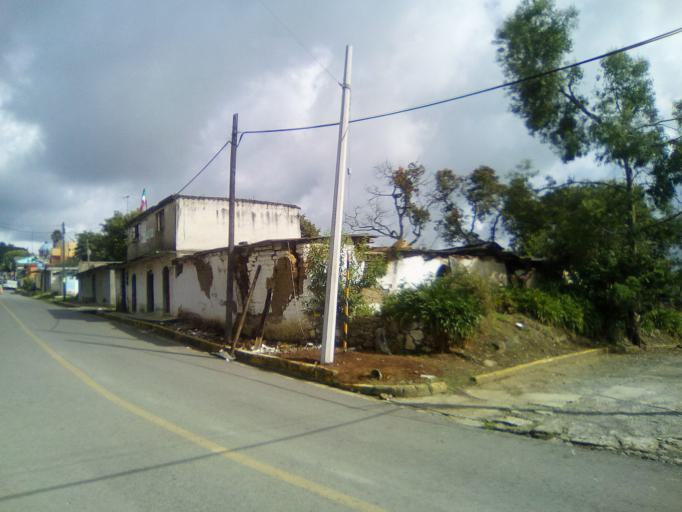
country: MX
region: Mexico
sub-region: Ocuilan
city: Santa Ana
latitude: 18.9887
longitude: -99.4159
